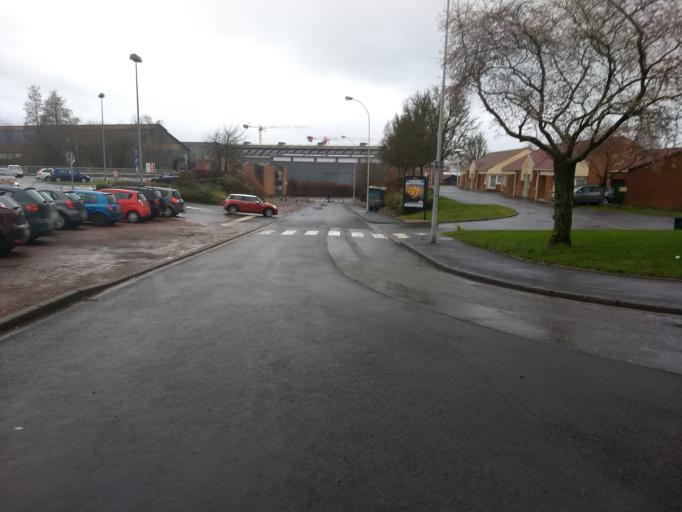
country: FR
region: Nord-Pas-de-Calais
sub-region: Departement du Pas-de-Calais
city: Arras
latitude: 50.2920
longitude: 2.7870
